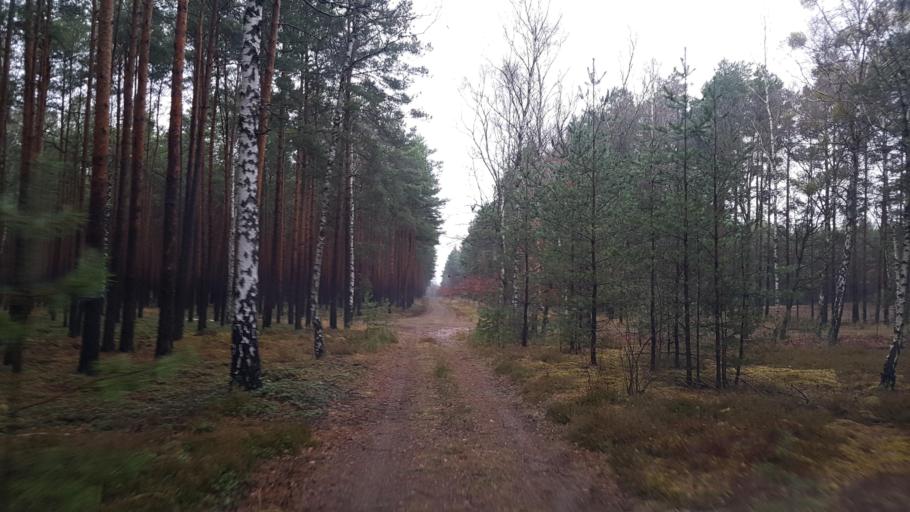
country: DE
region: Brandenburg
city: Grossraschen
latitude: 51.6288
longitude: 13.9676
